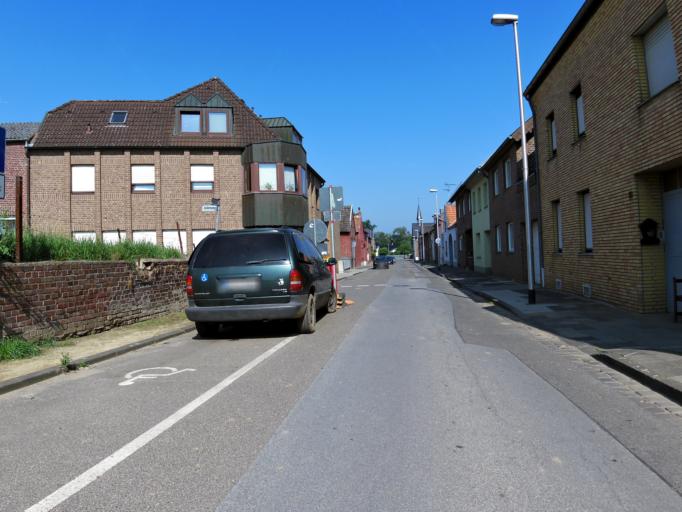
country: DE
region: North Rhine-Westphalia
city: Huckelhoven
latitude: 51.0118
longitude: 6.2286
